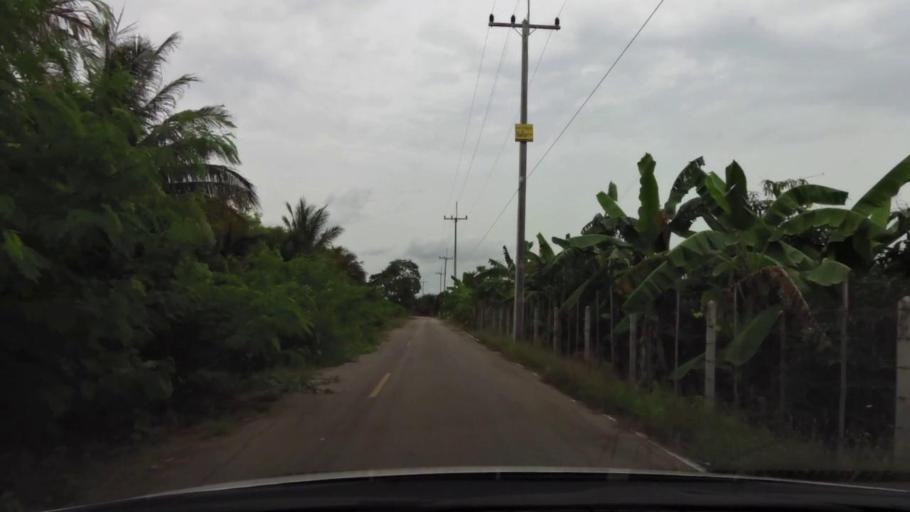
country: TH
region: Samut Sakhon
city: Ban Phaeo
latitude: 13.5852
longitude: 100.0368
